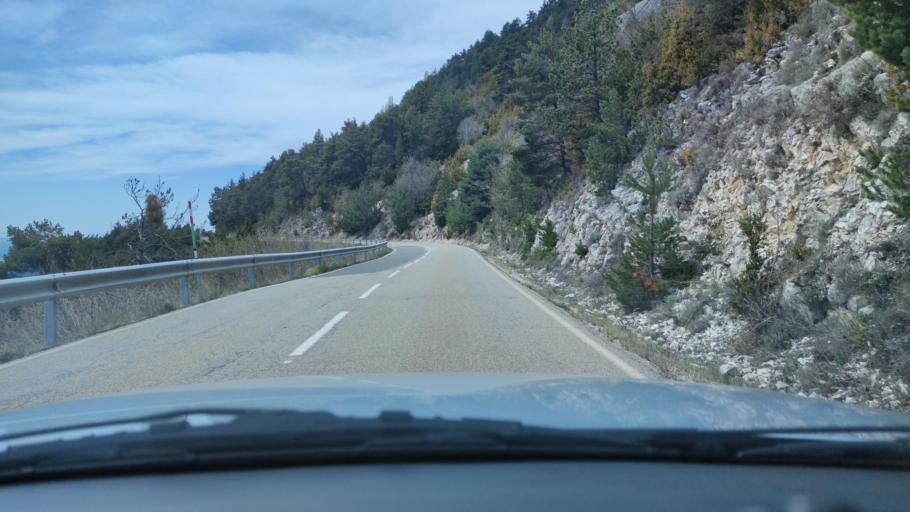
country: ES
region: Catalonia
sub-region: Provincia de Lleida
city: Gosol
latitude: 42.1587
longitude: 1.5744
